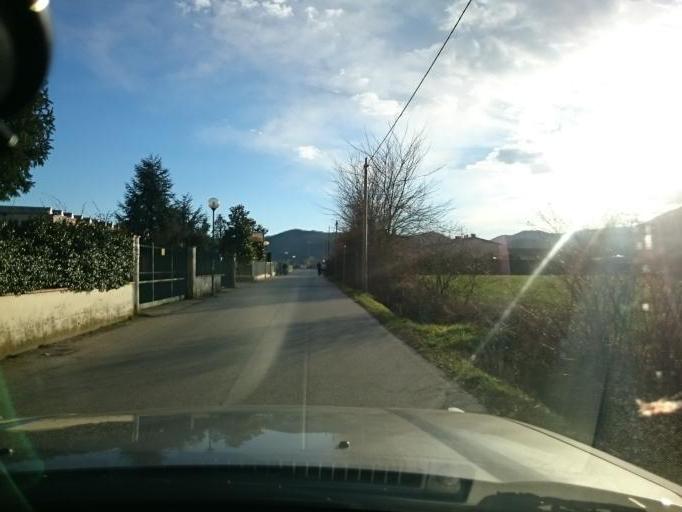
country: IT
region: Veneto
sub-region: Provincia di Padova
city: Torreglia
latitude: 45.3372
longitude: 11.7465
